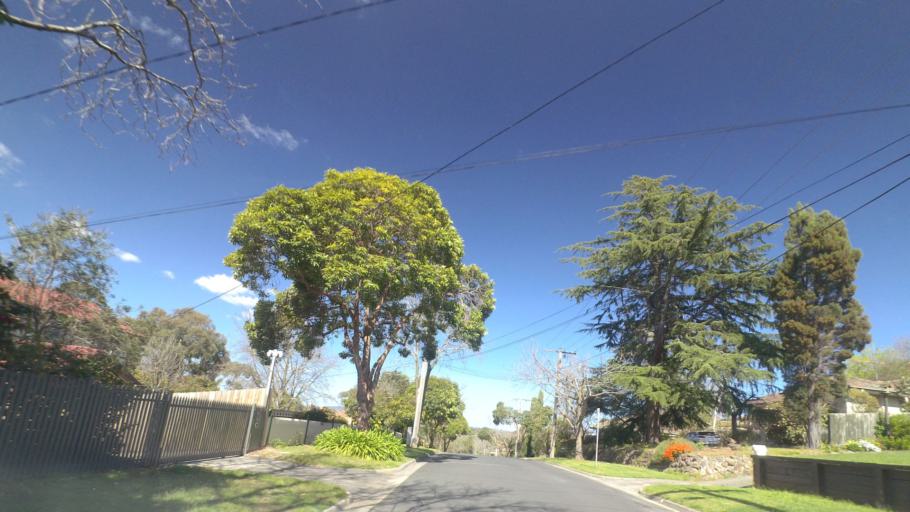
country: AU
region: Victoria
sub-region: Maroondah
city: Heathmont
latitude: -37.8325
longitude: 145.2433
